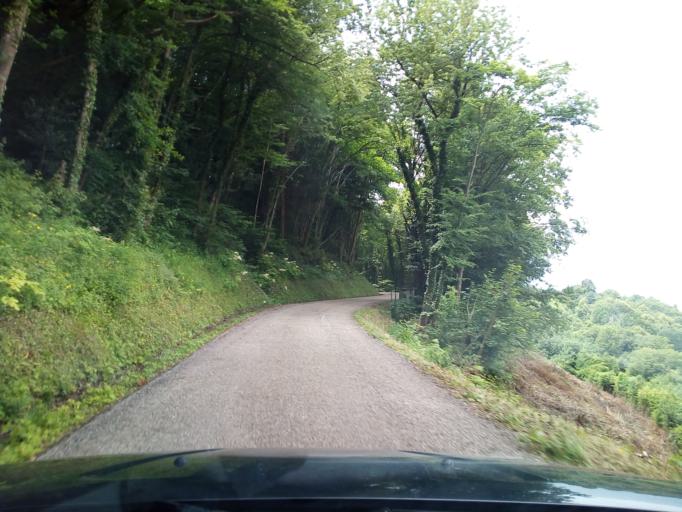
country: FR
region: Rhone-Alpes
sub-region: Departement de l'Isere
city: Gieres
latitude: 45.1616
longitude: 5.7857
